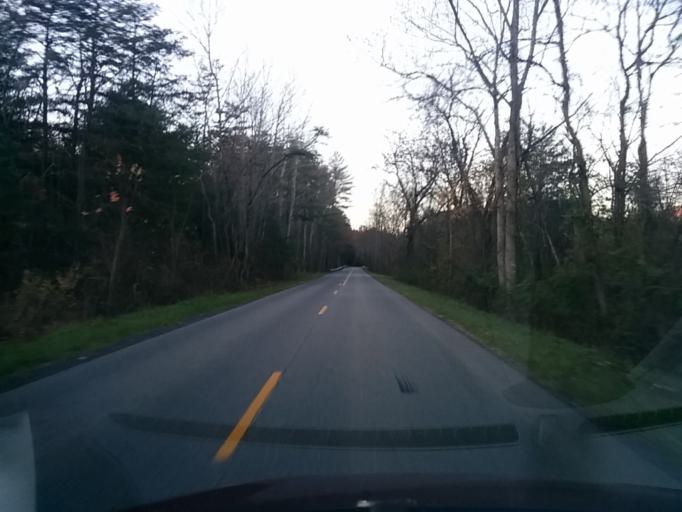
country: US
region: Virginia
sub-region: City of Lexington
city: Lexington
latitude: 37.9609
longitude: -79.5288
